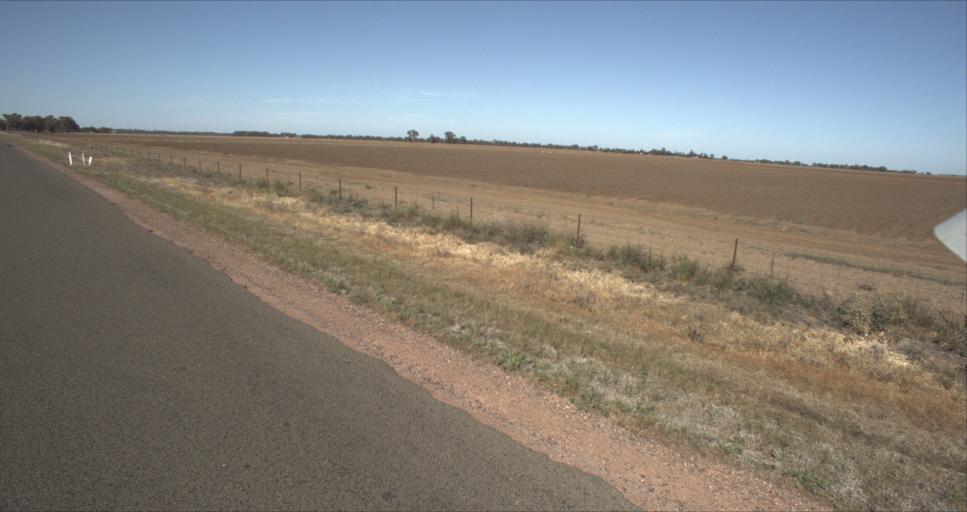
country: AU
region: New South Wales
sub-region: Leeton
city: Leeton
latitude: -34.5699
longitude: 146.2637
